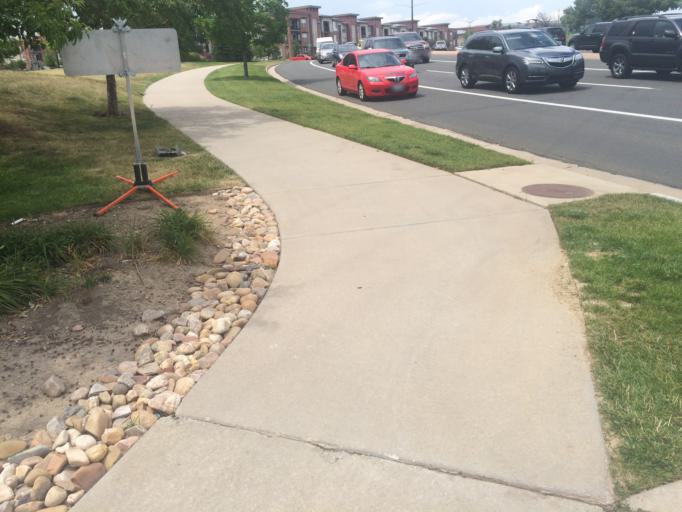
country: US
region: Colorado
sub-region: Broomfield County
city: Broomfield
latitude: 39.8914
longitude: -105.0715
